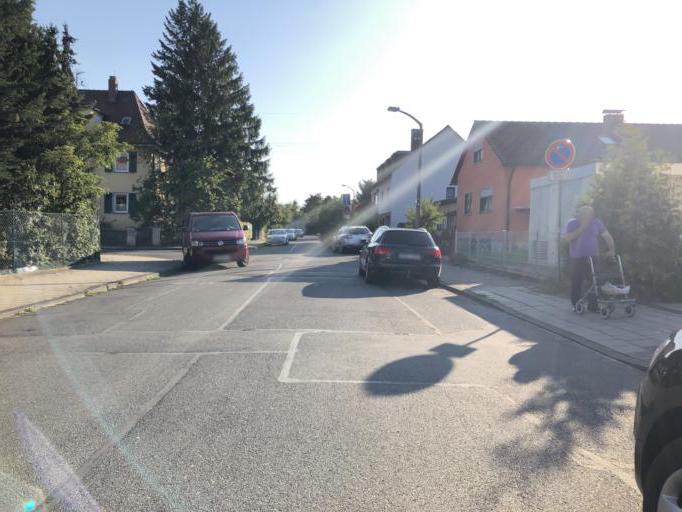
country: DE
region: Bavaria
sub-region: Regierungsbezirk Mittelfranken
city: Erlangen
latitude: 49.5874
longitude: 10.9917
